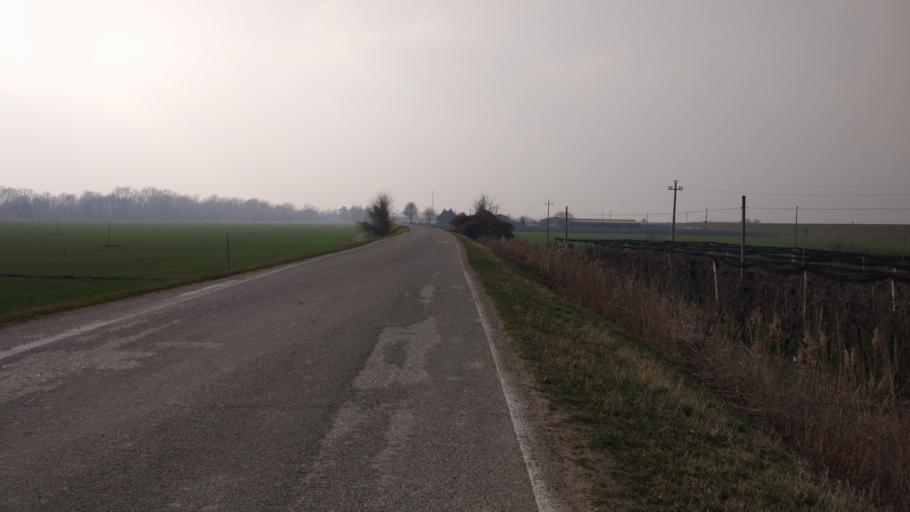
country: IT
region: Veneto
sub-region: Provincia di Verona
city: Zevio
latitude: 45.3828
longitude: 11.1488
